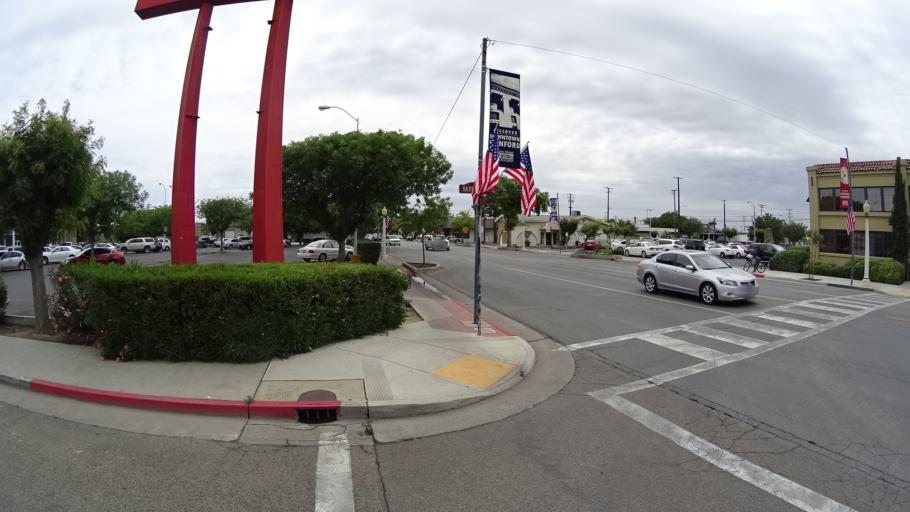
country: US
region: California
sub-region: Kings County
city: Hanford
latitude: 36.3258
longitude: -119.6517
